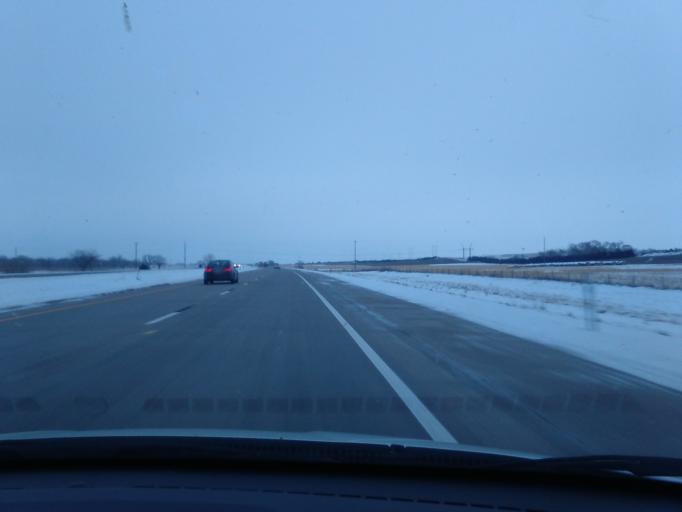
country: US
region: Nebraska
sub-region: Lincoln County
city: Sutherland
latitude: 41.1075
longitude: -101.3876
